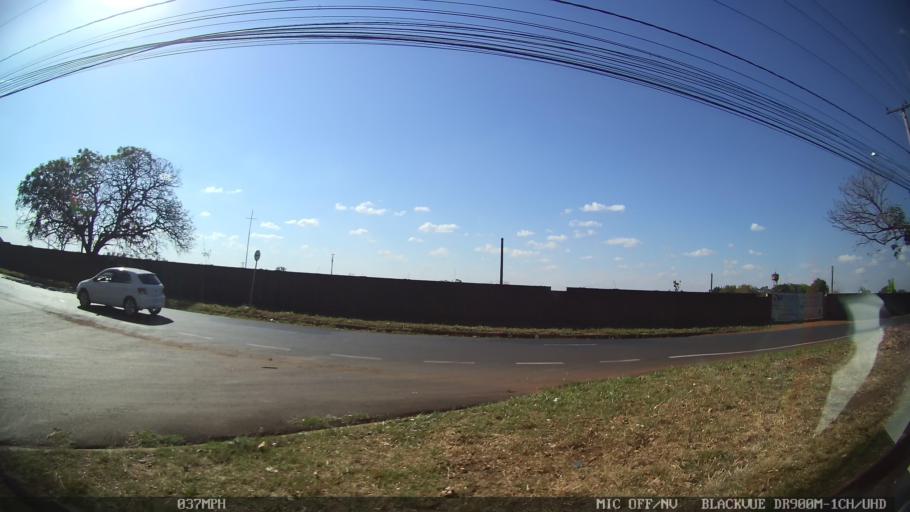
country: BR
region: Sao Paulo
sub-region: Ribeirao Preto
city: Ribeirao Preto
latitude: -21.1509
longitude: -47.7651
